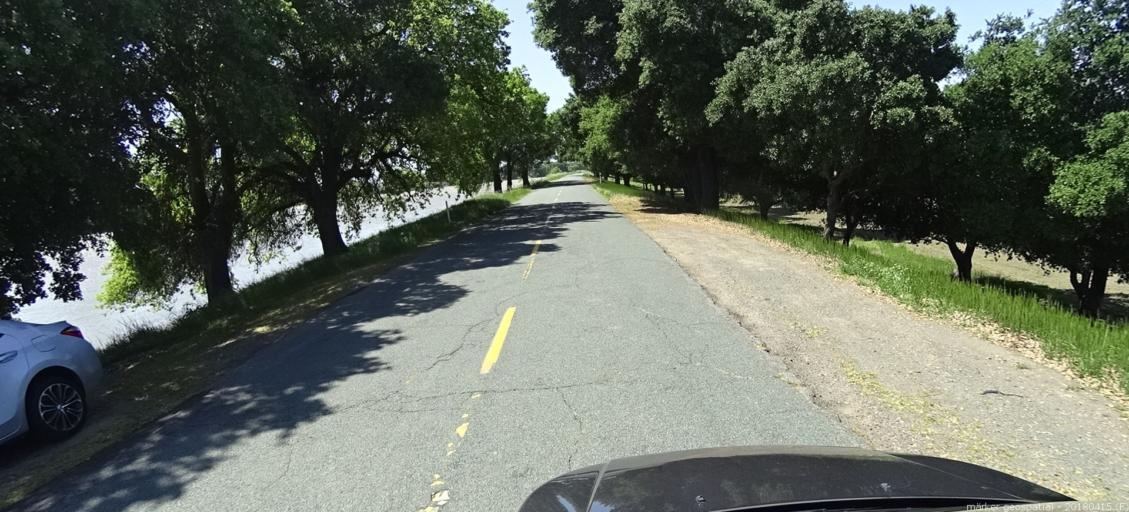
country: US
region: California
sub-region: Solano County
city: Rio Vista
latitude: 38.1673
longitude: -121.6004
